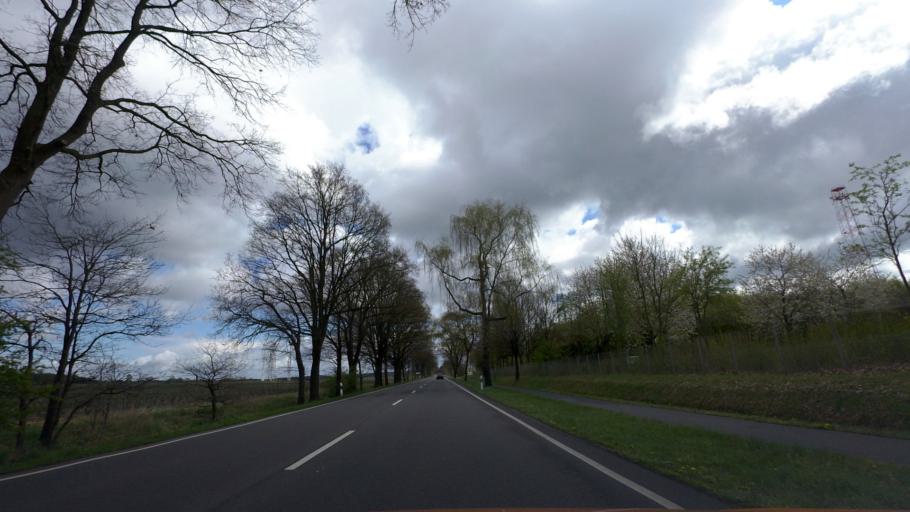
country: DE
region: Lower Saxony
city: Sottrum
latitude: 53.1153
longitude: 9.2454
